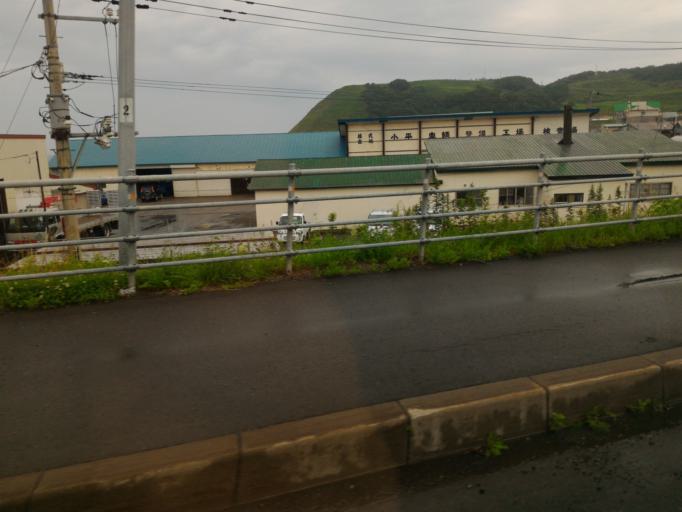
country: JP
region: Hokkaido
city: Rumoi
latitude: 44.0246
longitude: 141.6659
